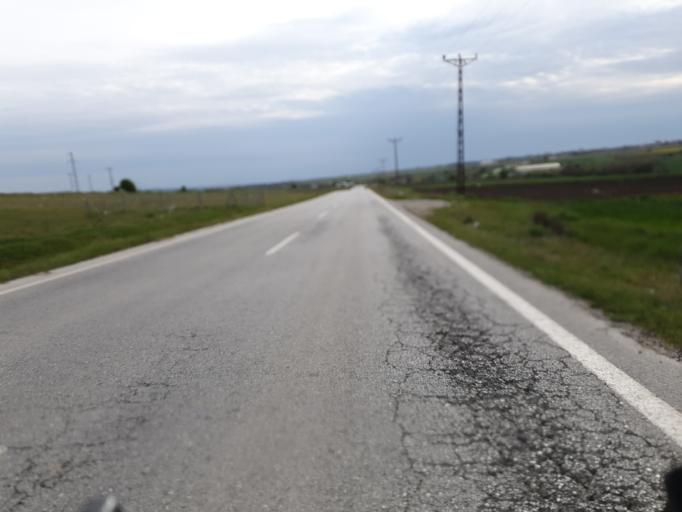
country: TR
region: Tekirdag
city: Velimese
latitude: 41.2936
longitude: 27.9313
